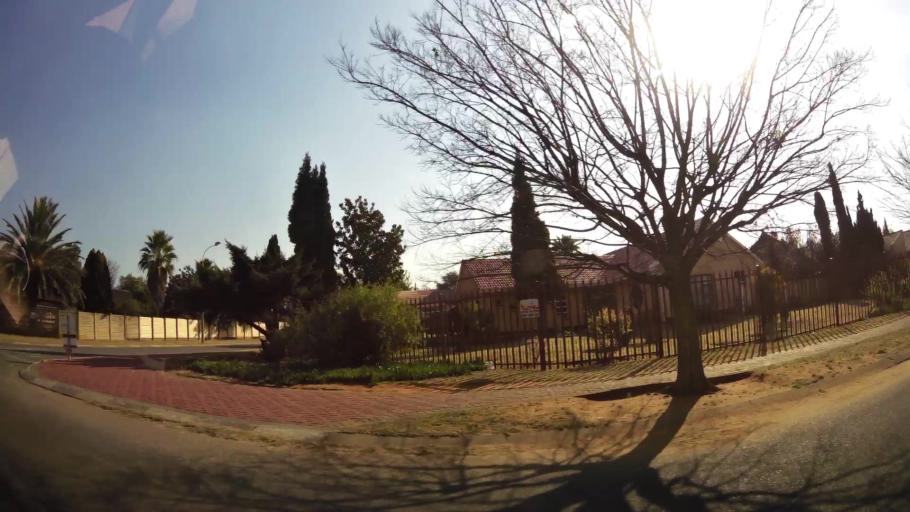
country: ZA
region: Gauteng
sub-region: West Rand District Municipality
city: Randfontein
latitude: -26.1791
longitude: 27.6839
